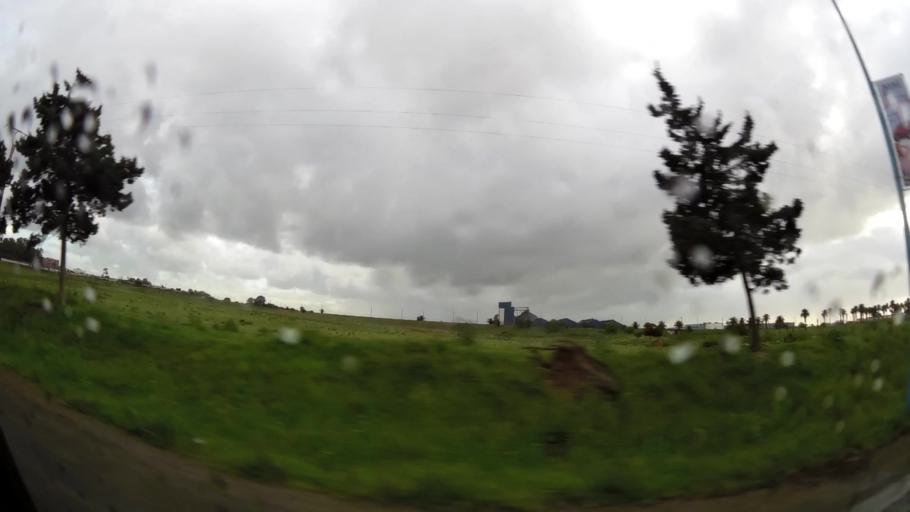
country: MA
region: Grand Casablanca
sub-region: Mohammedia
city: Mohammedia
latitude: 33.6742
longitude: -7.4078
